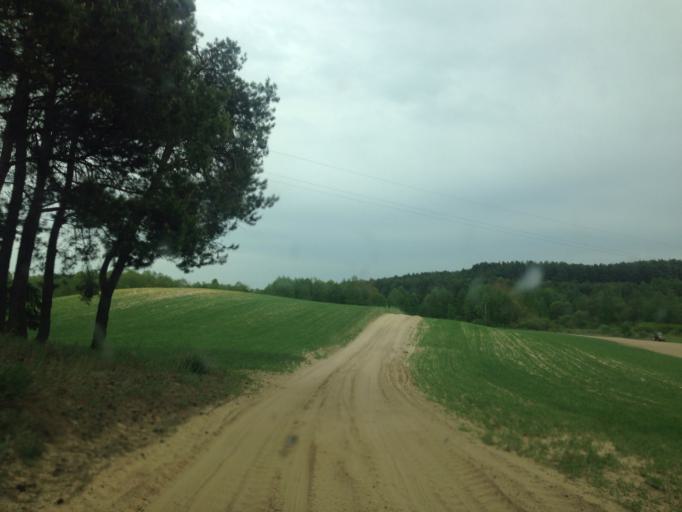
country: PL
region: Kujawsko-Pomorskie
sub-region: Powiat brodnicki
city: Bartniczka
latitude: 53.2766
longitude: 19.6077
